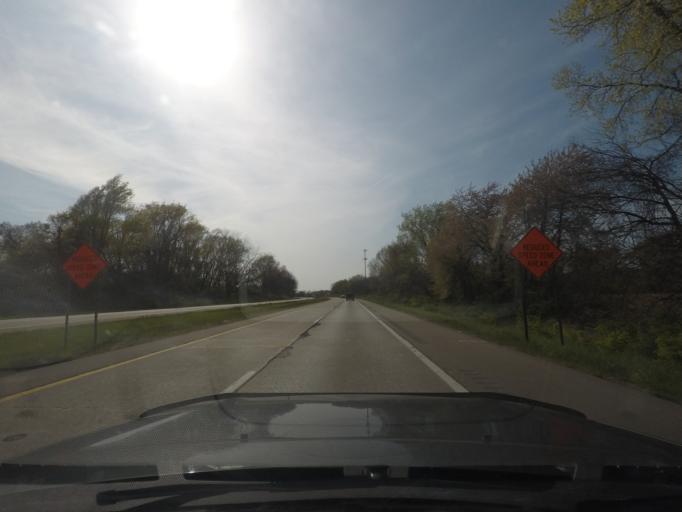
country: US
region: Michigan
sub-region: Berrien County
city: Niles
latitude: 41.8043
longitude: -86.2916
